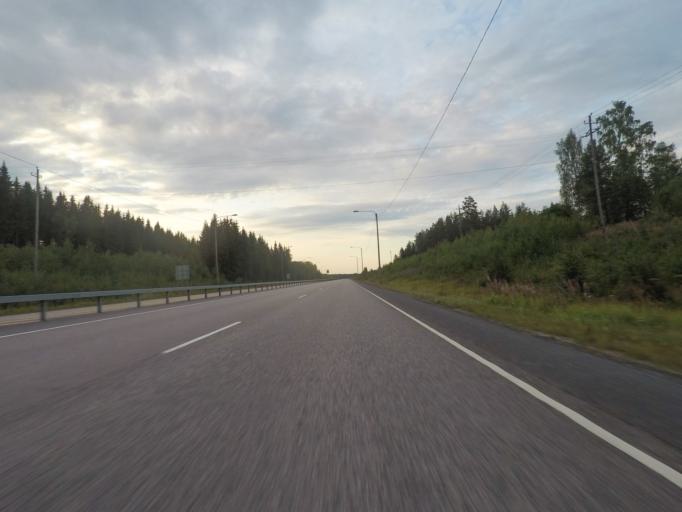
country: FI
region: Central Finland
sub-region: Joutsa
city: Joutsa
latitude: 61.7986
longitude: 26.0940
